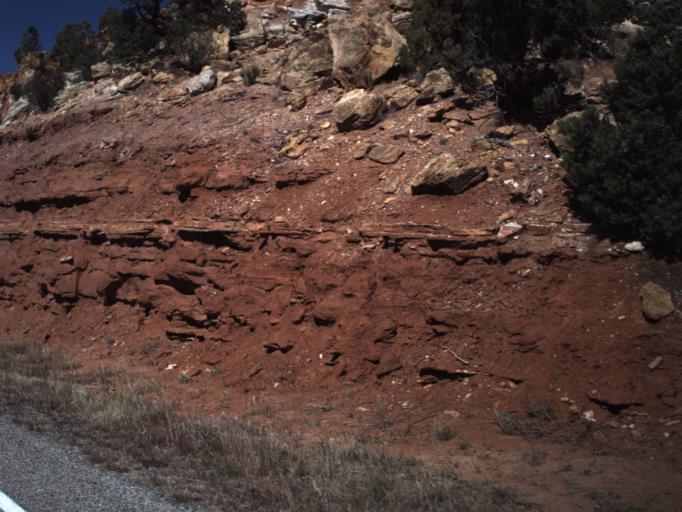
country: US
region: Utah
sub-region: Wayne County
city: Loa
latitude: 37.8926
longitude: -111.4536
